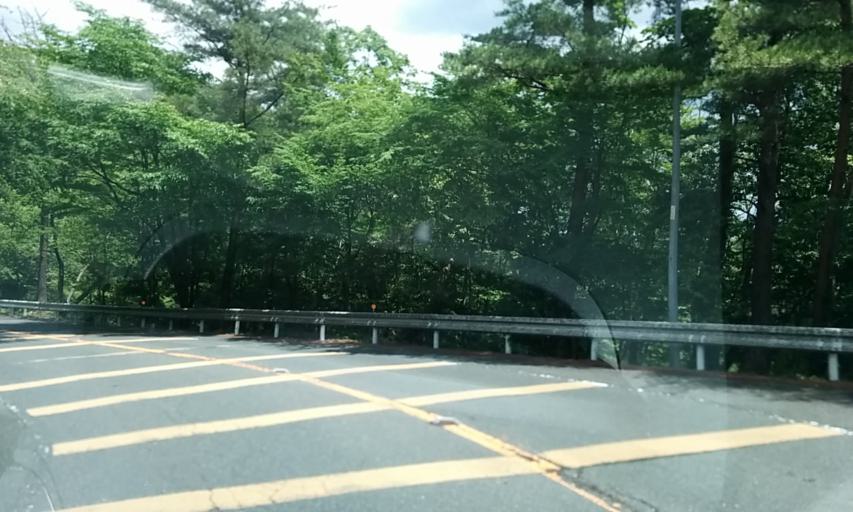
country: JP
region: Kyoto
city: Kameoka
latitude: 35.0369
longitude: 135.4059
